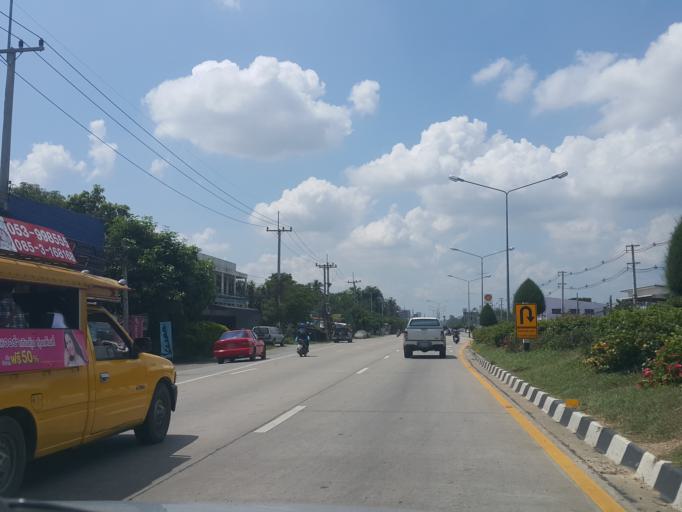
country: TH
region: Chiang Mai
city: San Sai
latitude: 18.8199
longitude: 99.0399
